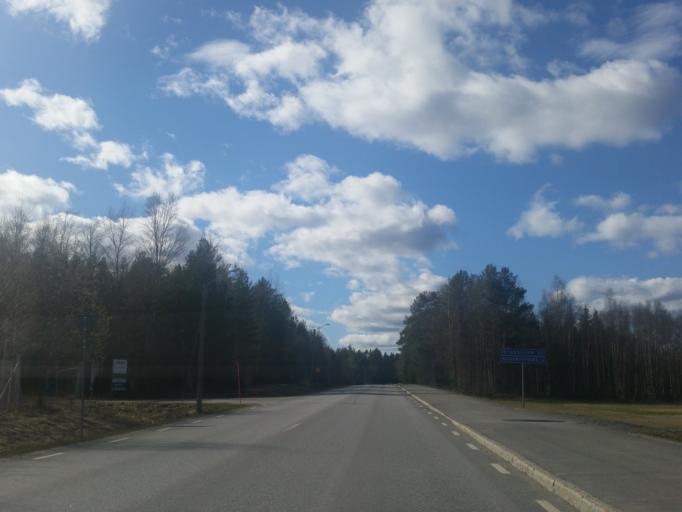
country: SE
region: Vaesterbotten
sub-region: Robertsfors Kommun
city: Robertsfors
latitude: 64.1688
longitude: 20.9231
